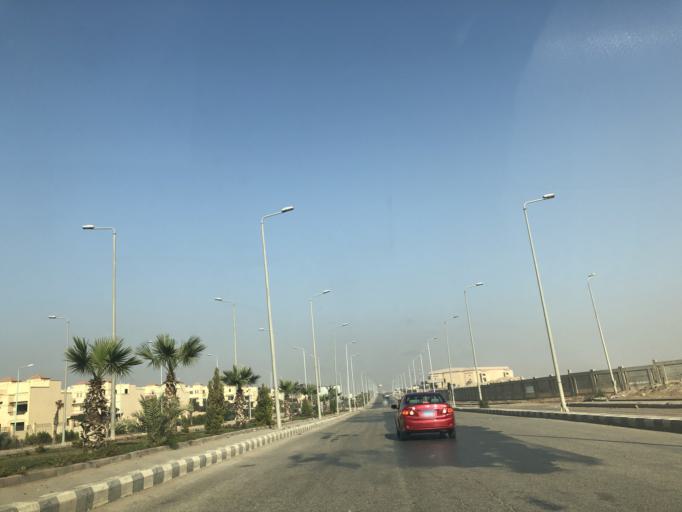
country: EG
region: Al Jizah
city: Madinat Sittah Uktubar
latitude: 29.9492
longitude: 31.0689
